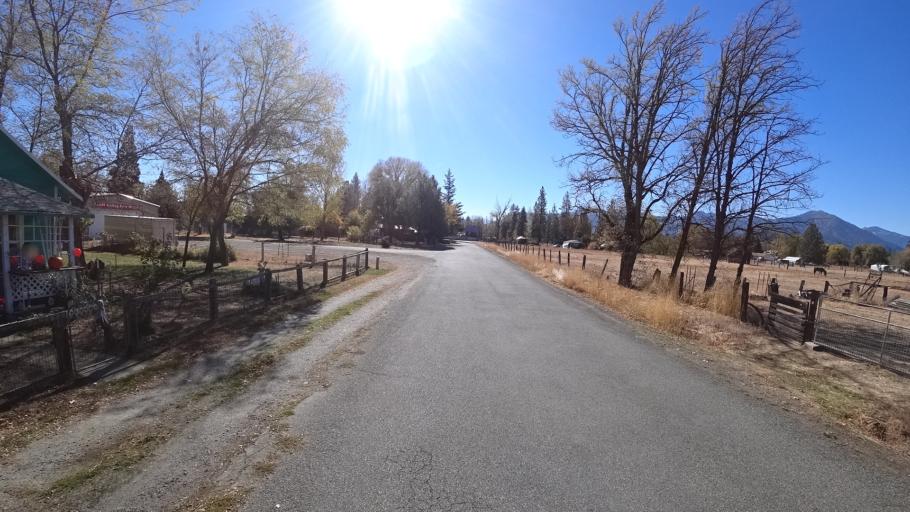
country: US
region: California
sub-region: Siskiyou County
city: Yreka
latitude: 41.5501
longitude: -122.9078
